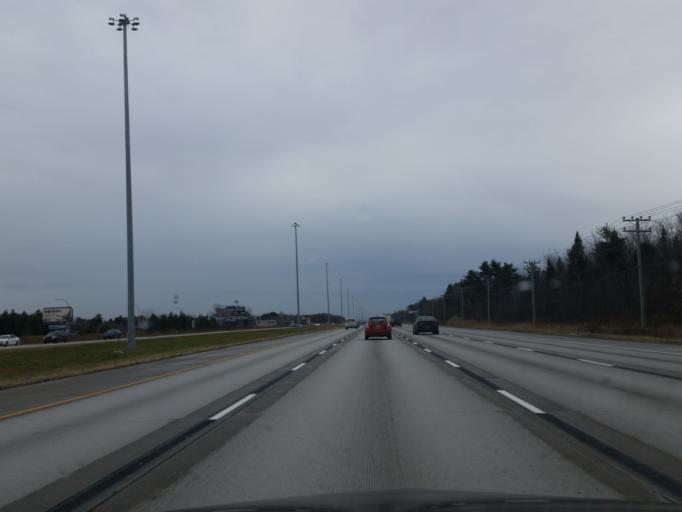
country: CA
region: Quebec
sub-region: Laurentides
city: Blainville
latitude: 45.6658
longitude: -73.8978
